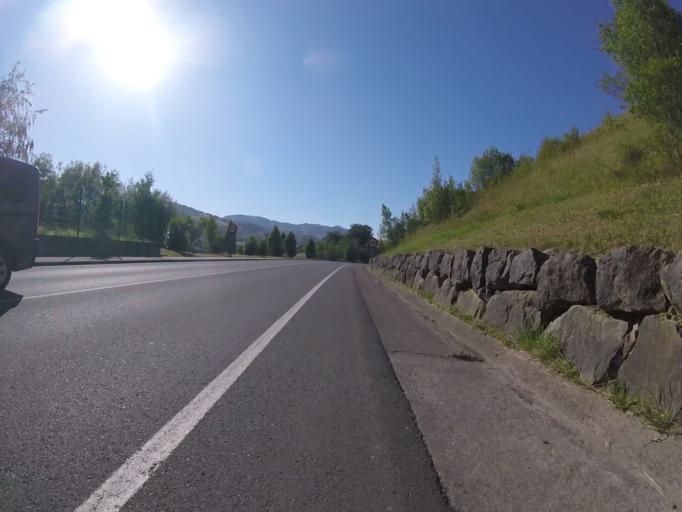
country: ES
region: Basque Country
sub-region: Provincia de Guipuzcoa
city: Azpeitia
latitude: 43.1750
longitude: -2.2590
